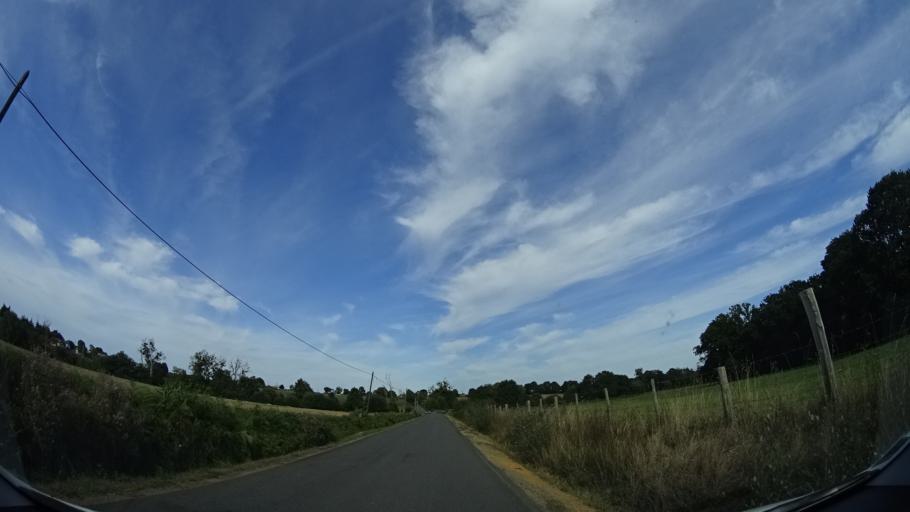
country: FR
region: Brittany
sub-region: Departement d'Ille-et-Vilaine
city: Javene
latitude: 48.3368
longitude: -1.2350
